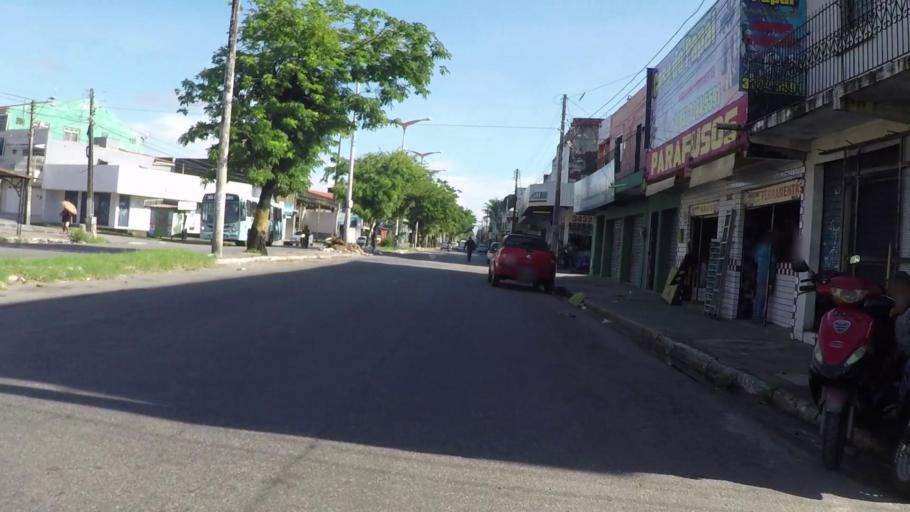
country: BR
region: Ceara
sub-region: Fortaleza
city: Fortaleza
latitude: -3.7226
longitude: -38.5865
